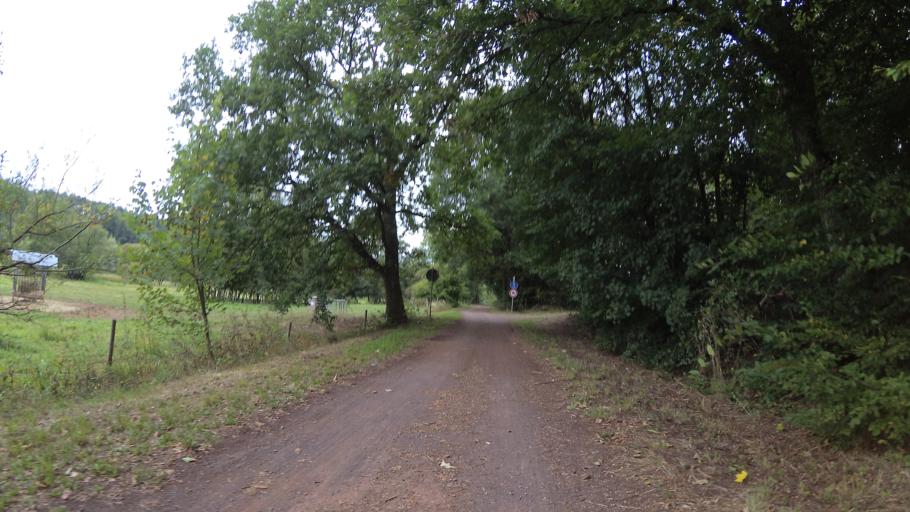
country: DE
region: Saarland
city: Wadern
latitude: 49.5290
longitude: 6.9462
